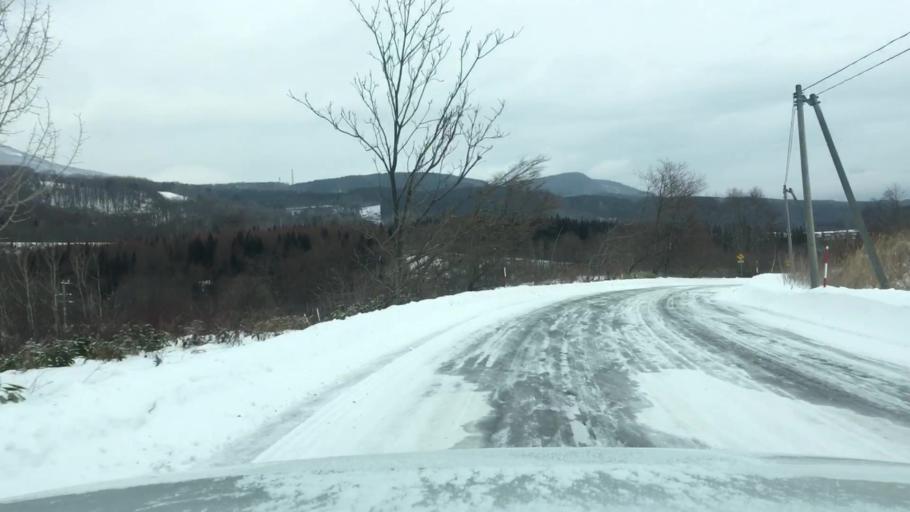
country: JP
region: Iwate
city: Shizukuishi
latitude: 39.9347
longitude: 141.0015
